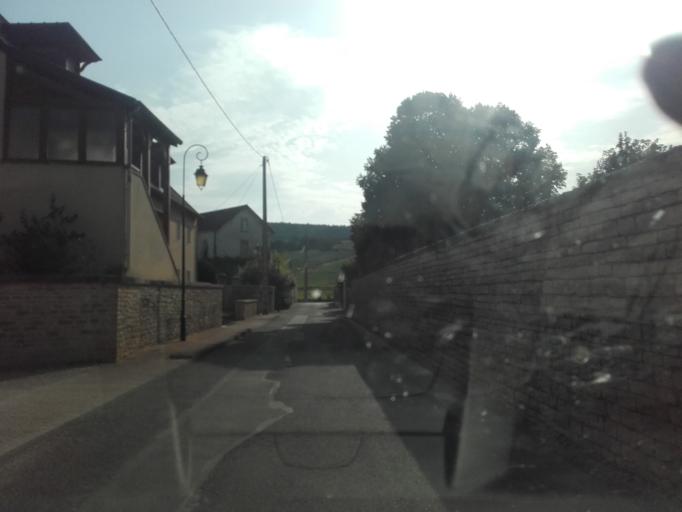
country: FR
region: Bourgogne
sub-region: Departement de la Cote-d'Or
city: Meursault
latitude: 46.9777
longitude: 4.7671
